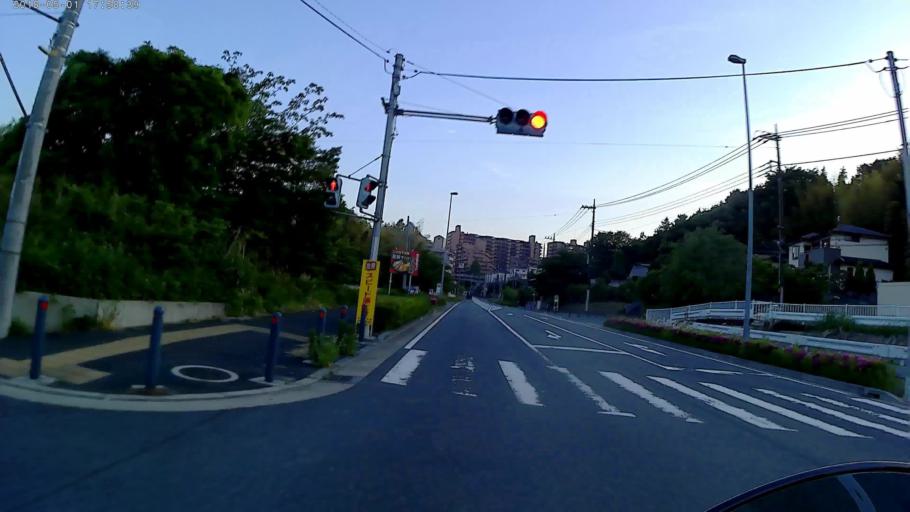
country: JP
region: Kanagawa
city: Yokohama
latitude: 35.5446
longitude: 139.5890
